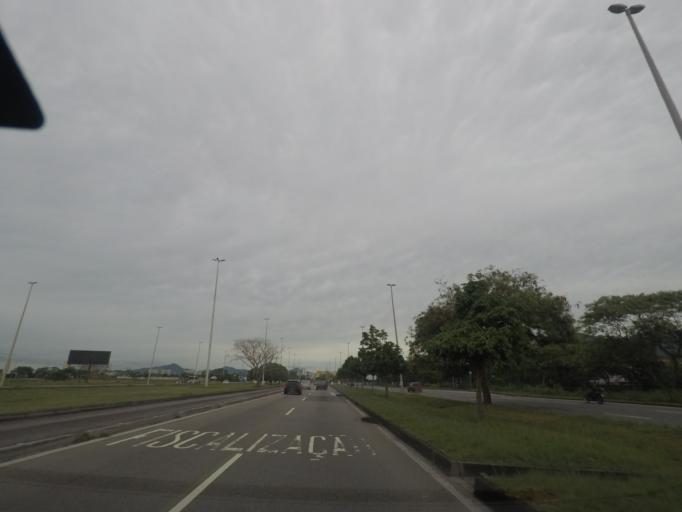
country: BR
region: Rio de Janeiro
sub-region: Nilopolis
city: Nilopolis
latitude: -22.9999
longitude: -43.4022
